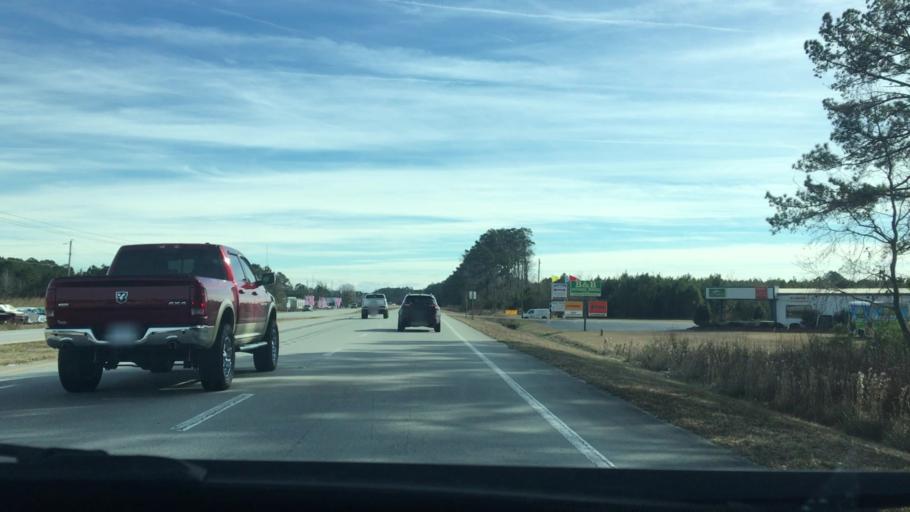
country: US
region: North Carolina
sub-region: Carteret County
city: Newport
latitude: 34.7561
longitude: -76.8475
